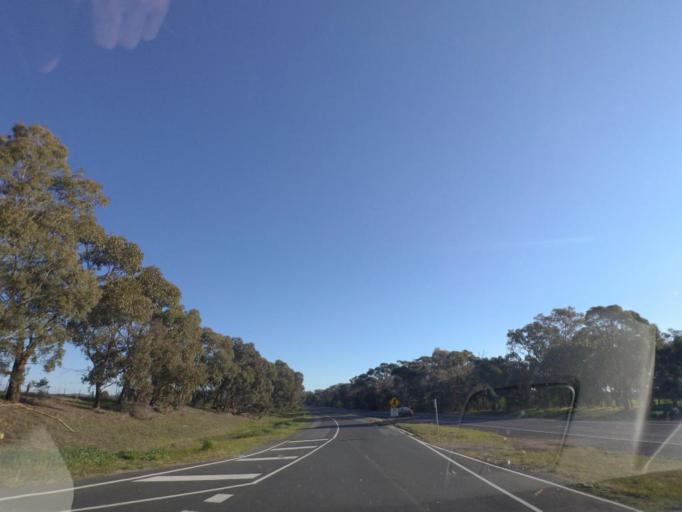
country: AU
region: Victoria
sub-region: Greater Shepparton
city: Shepparton
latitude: -36.7823
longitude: 145.4995
